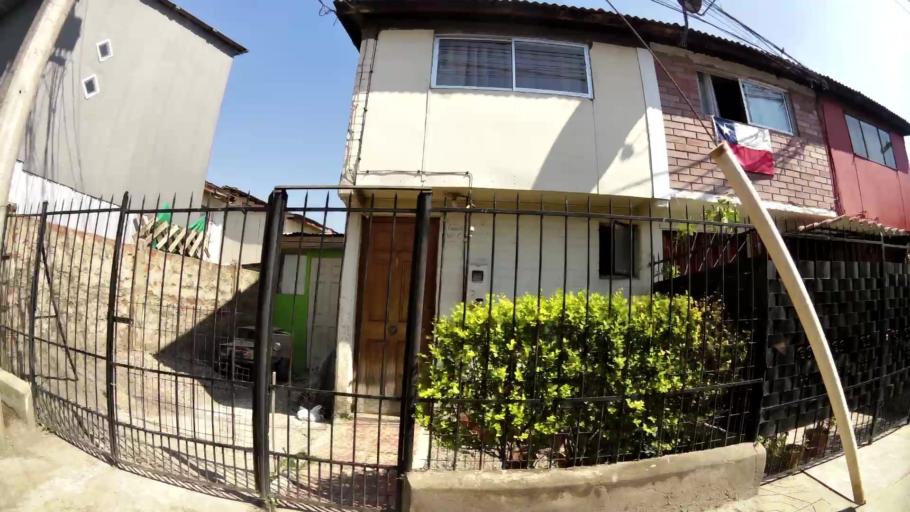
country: CL
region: Santiago Metropolitan
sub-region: Provincia de Santiago
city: La Pintana
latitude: -33.5518
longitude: -70.6073
